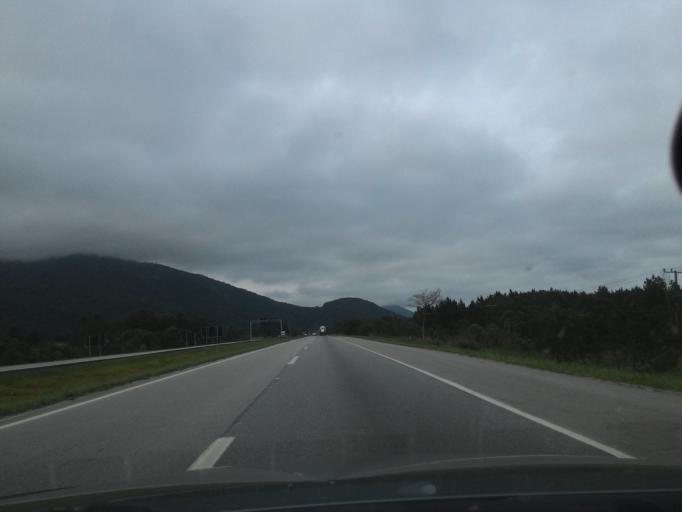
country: BR
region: Santa Catarina
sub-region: Florianopolis
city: Pantano do Sul
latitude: -27.8760
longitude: -48.6468
